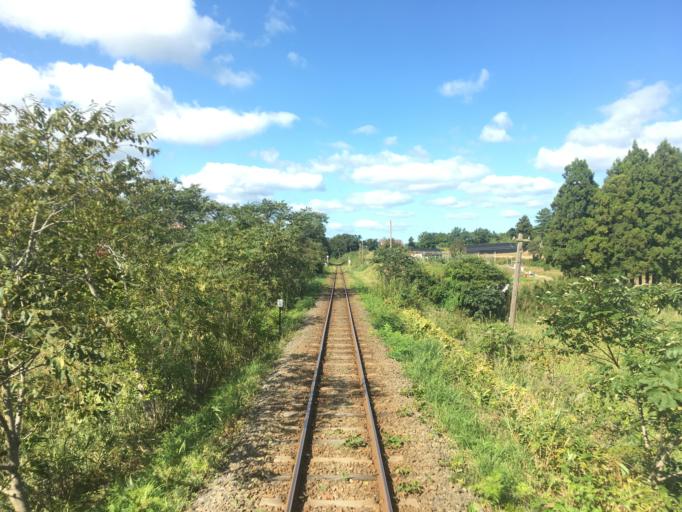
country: JP
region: Aomori
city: Goshogawara
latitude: 40.9565
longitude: 140.4435
